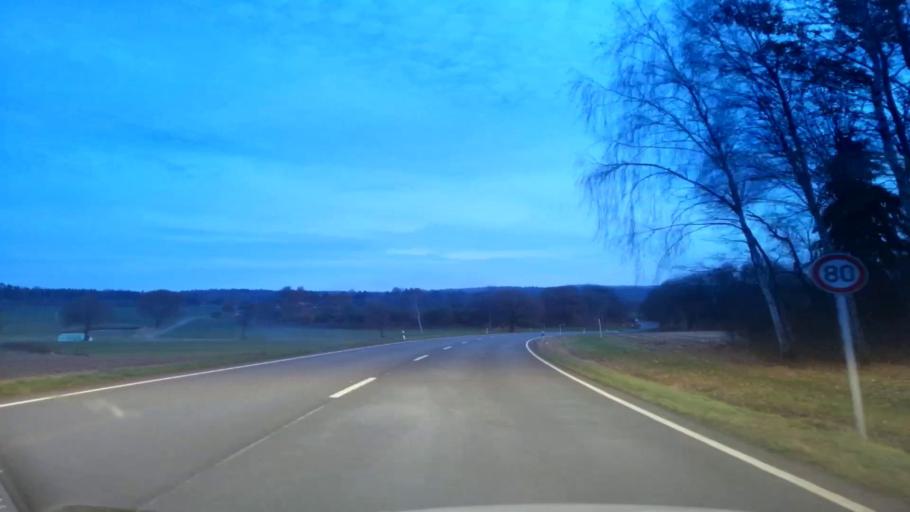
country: DE
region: Bavaria
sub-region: Upper Palatinate
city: Pechbrunn
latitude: 49.9753
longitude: 12.1484
